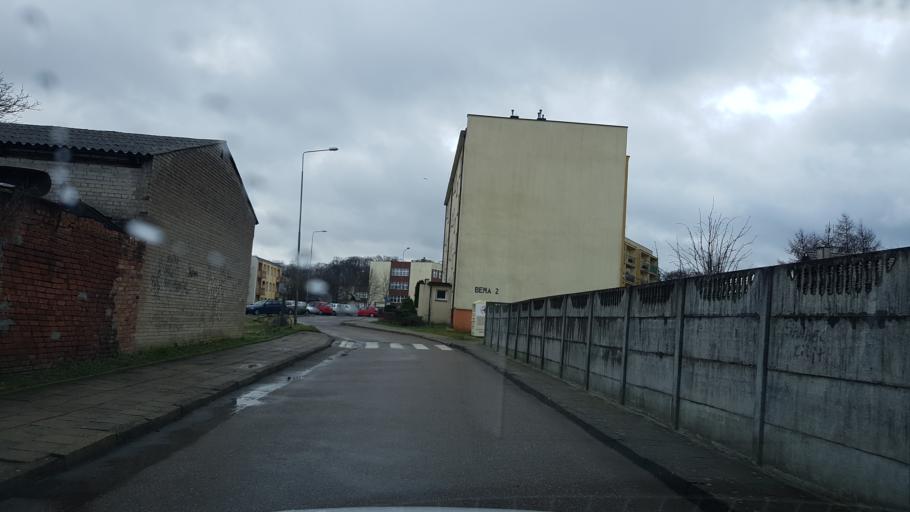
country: PL
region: West Pomeranian Voivodeship
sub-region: Powiat drawski
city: Czaplinek
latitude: 53.5574
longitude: 16.2362
